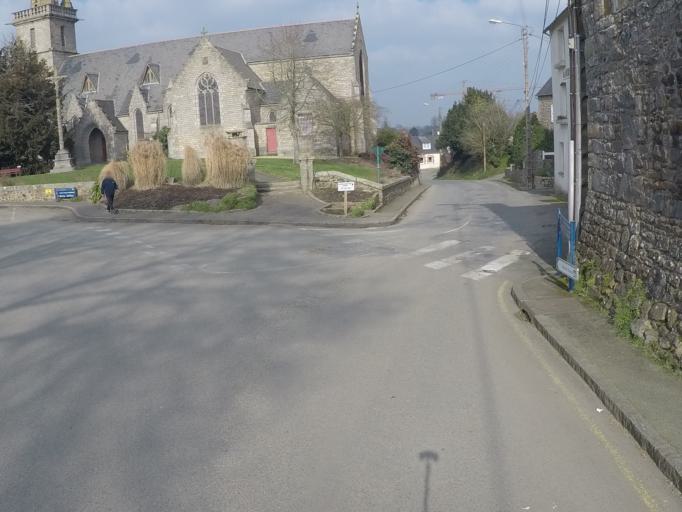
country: FR
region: Brittany
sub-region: Departement des Cotes-d'Armor
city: Pommerit-le-Vicomte
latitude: 48.6194
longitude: -3.0871
